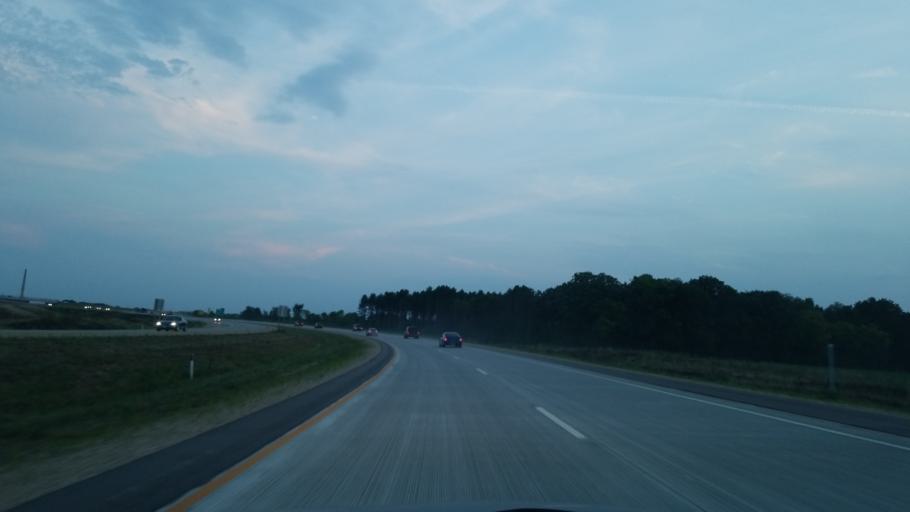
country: US
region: Minnesota
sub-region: Washington County
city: Stillwater
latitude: 45.0690
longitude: -92.7809
